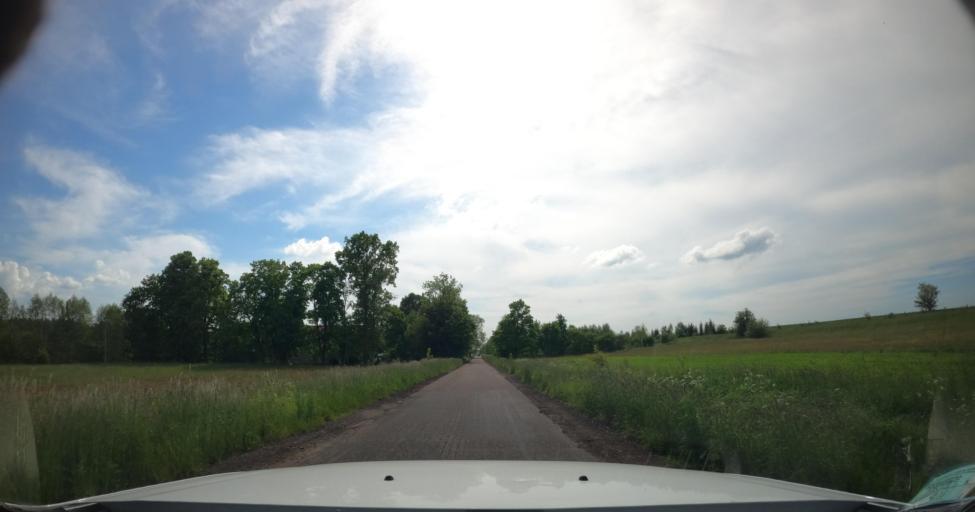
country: PL
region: Warmian-Masurian Voivodeship
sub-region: Powiat lidzbarski
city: Lidzbark Warminski
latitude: 54.1172
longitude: 20.5096
